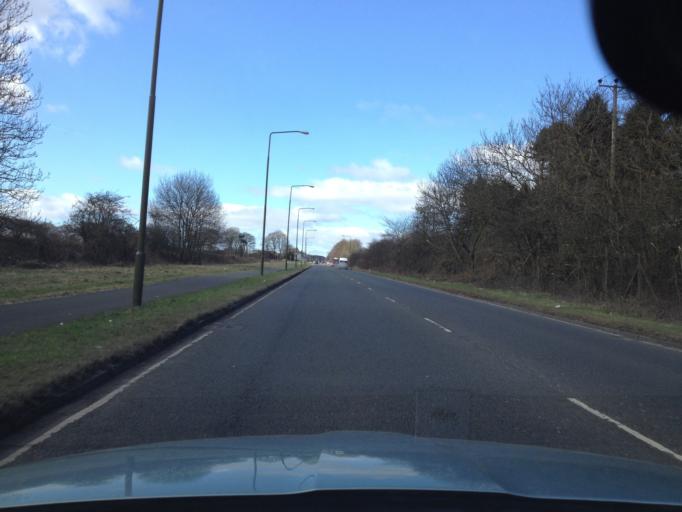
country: GB
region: Scotland
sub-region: West Lothian
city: Livingston
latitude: 55.9249
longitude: -3.5047
